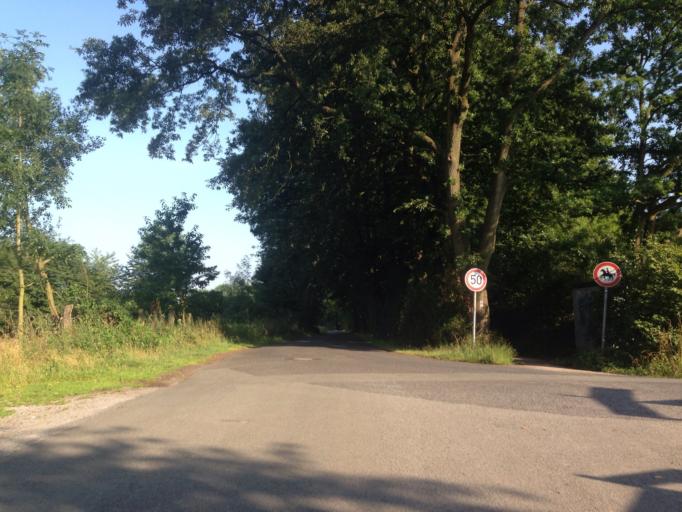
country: DE
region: North Rhine-Westphalia
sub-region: Regierungsbezirk Munster
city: Muenster
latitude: 51.9989
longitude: 7.5791
